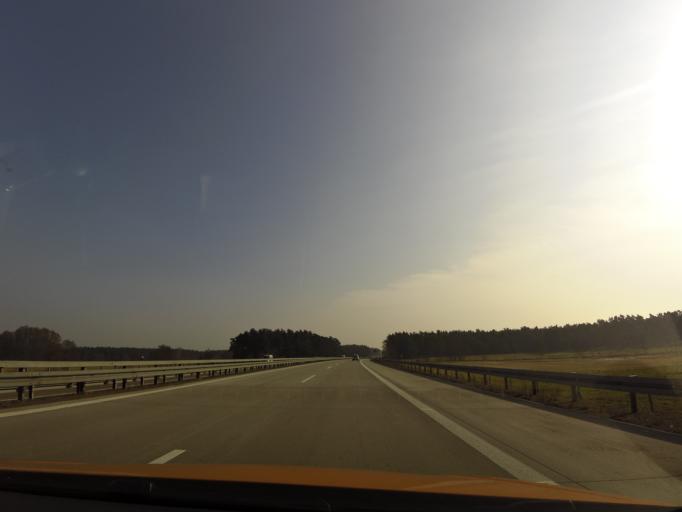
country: DE
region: Brandenburg
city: Briesen
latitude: 52.3347
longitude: 14.2519
